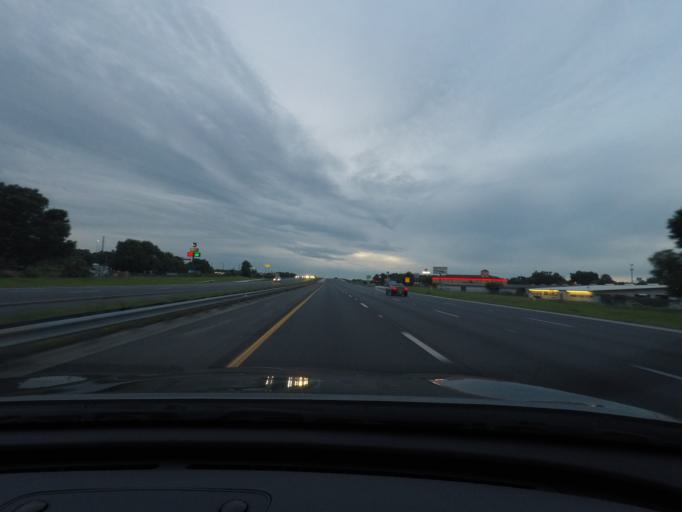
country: US
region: Florida
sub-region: Marion County
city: Belleview
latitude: 29.0216
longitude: -82.1559
